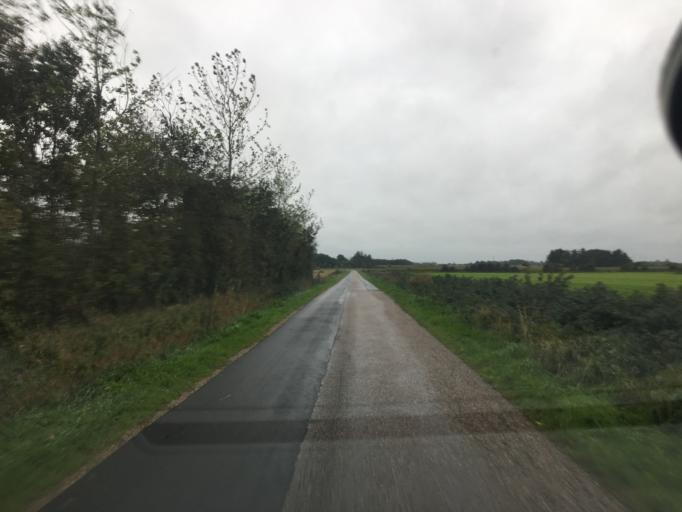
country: DE
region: Schleswig-Holstein
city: Ellhoft
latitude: 54.9448
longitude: 8.9983
